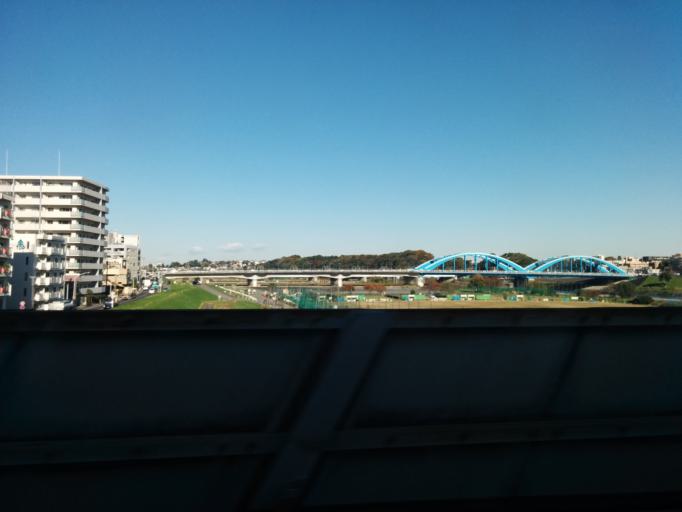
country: JP
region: Kanagawa
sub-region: Kawasaki-shi
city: Kawasaki
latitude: 35.5804
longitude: 139.6685
